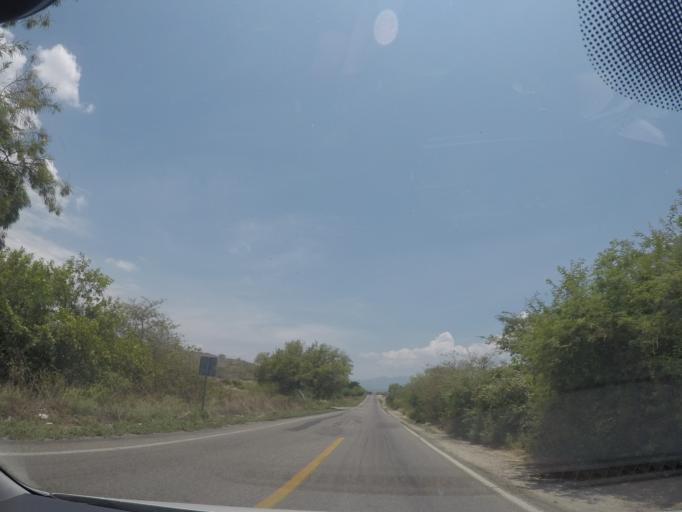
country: MX
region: Oaxaca
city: Santa Maria Jalapa del Marques
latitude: 16.4394
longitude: -95.4967
